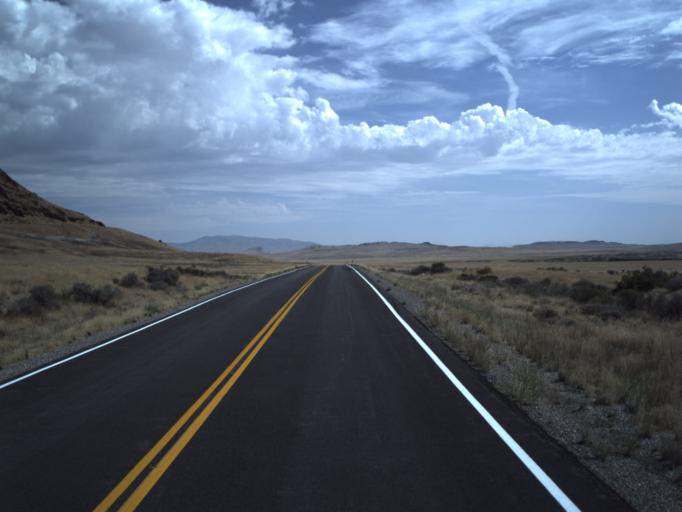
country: US
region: Utah
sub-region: Tooele County
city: Wendover
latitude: 41.3762
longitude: -114.0103
